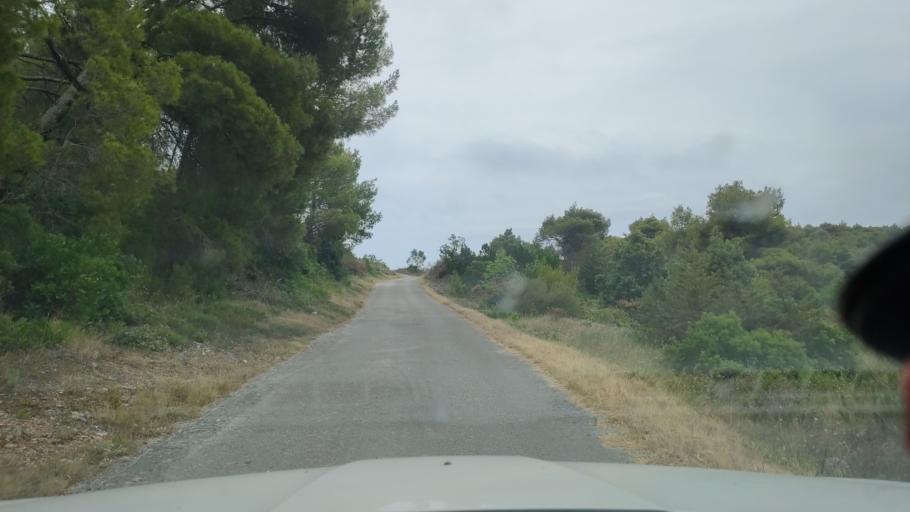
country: HR
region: Splitsko-Dalmatinska
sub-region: Grad Vis
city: Vis
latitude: 43.0298
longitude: 16.1679
